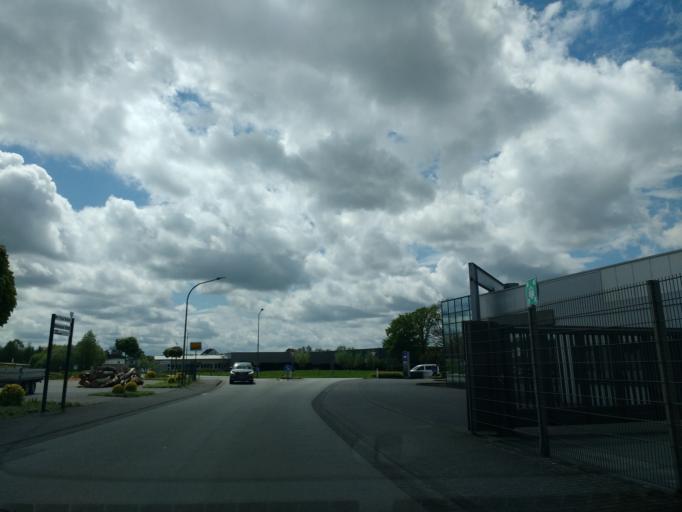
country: DE
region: North Rhine-Westphalia
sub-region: Regierungsbezirk Detmold
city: Oerlinghausen
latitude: 51.9094
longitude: 8.6773
